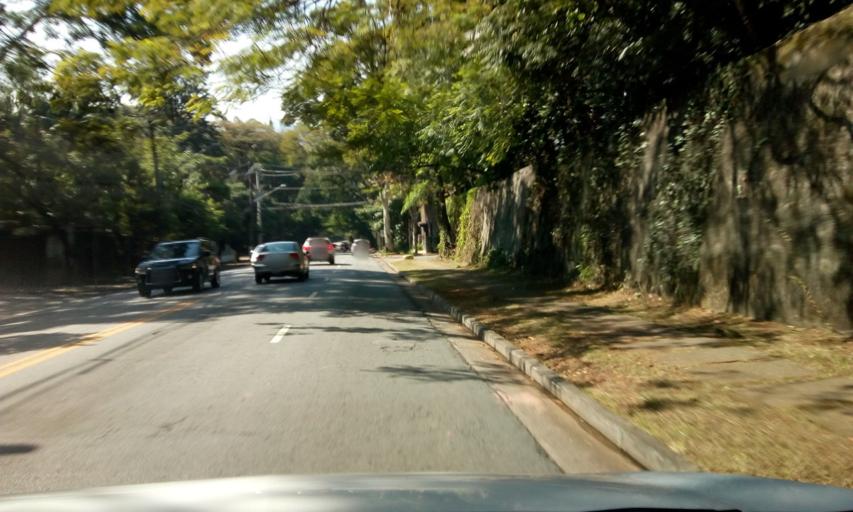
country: BR
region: Sao Paulo
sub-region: Sao Paulo
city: Sao Paulo
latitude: -23.5962
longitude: -46.7003
